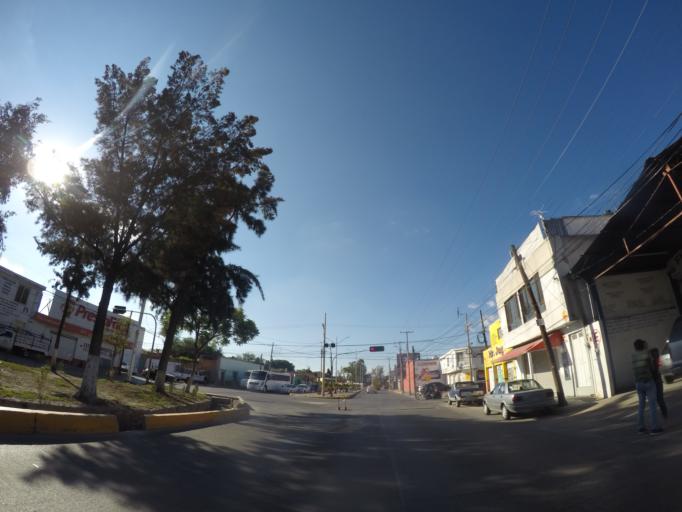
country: MX
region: San Luis Potosi
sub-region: San Luis Potosi
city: San Luis Potosi
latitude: 22.1698
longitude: -100.9814
